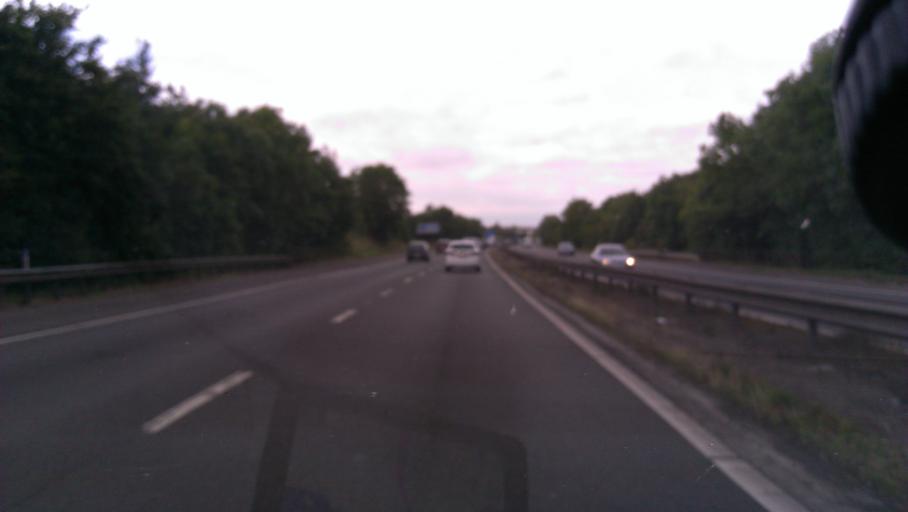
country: GB
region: England
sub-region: Cambridgeshire
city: Grantchester
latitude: 52.1720
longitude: 0.0854
